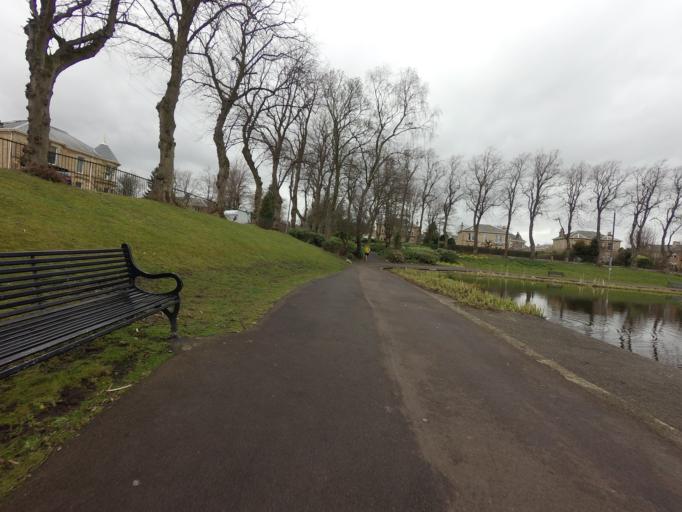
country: GB
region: Scotland
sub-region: East Renfrewshire
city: Giffnock
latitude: 55.8383
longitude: -4.2920
